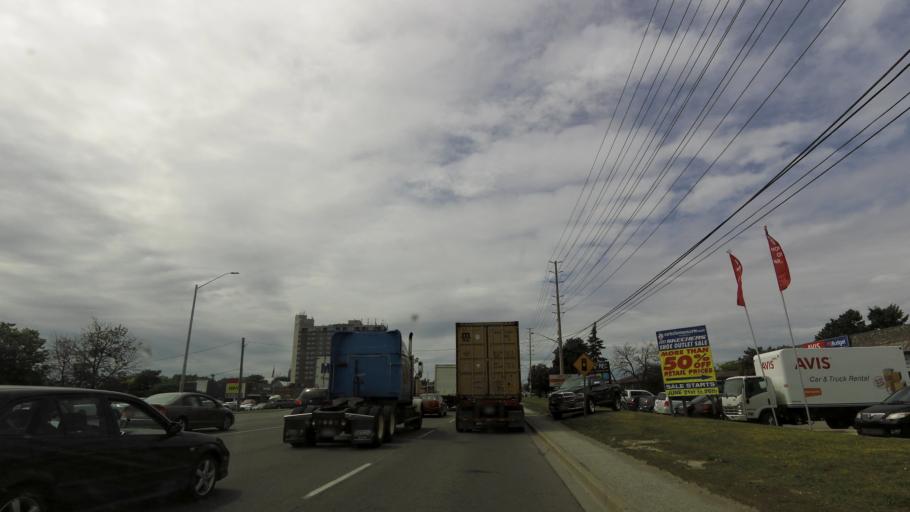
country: CA
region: Ontario
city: Etobicoke
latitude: 43.6414
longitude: -79.6283
